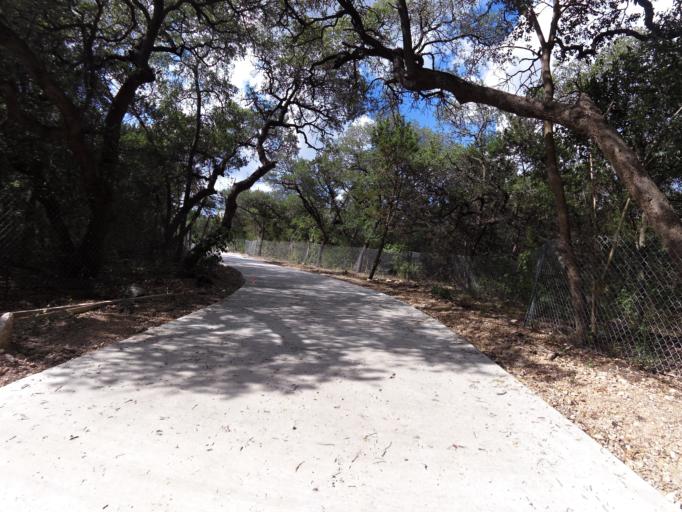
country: US
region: Texas
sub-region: Bexar County
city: Shavano Park
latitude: 29.5969
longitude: -98.5956
